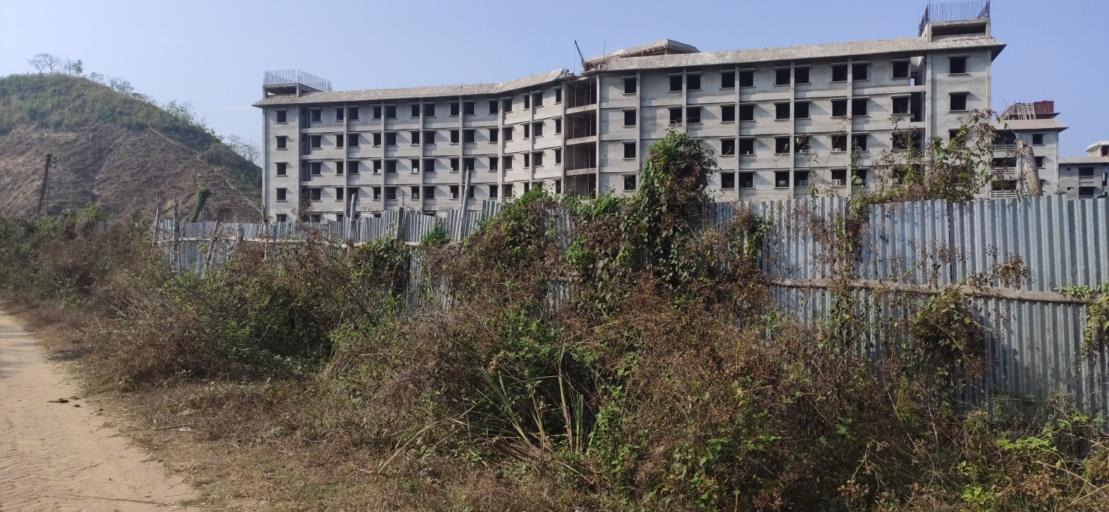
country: BD
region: Chittagong
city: Chittagong
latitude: 22.4764
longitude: 91.7843
